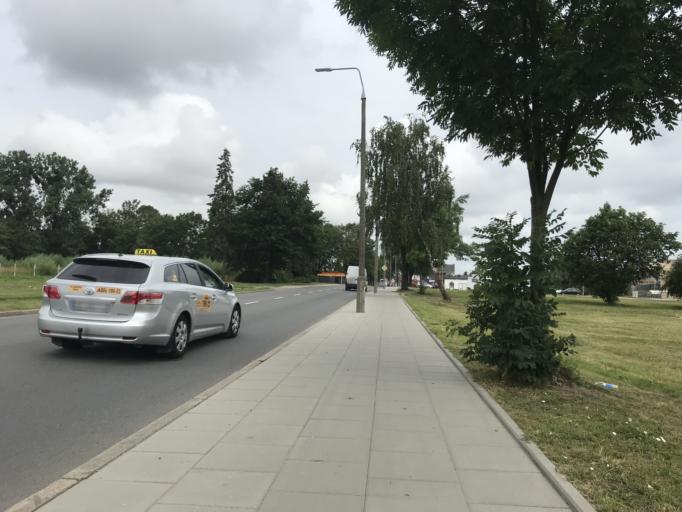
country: PL
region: Warmian-Masurian Voivodeship
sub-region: Powiat elblaski
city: Elblag
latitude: 54.1569
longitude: 19.3910
